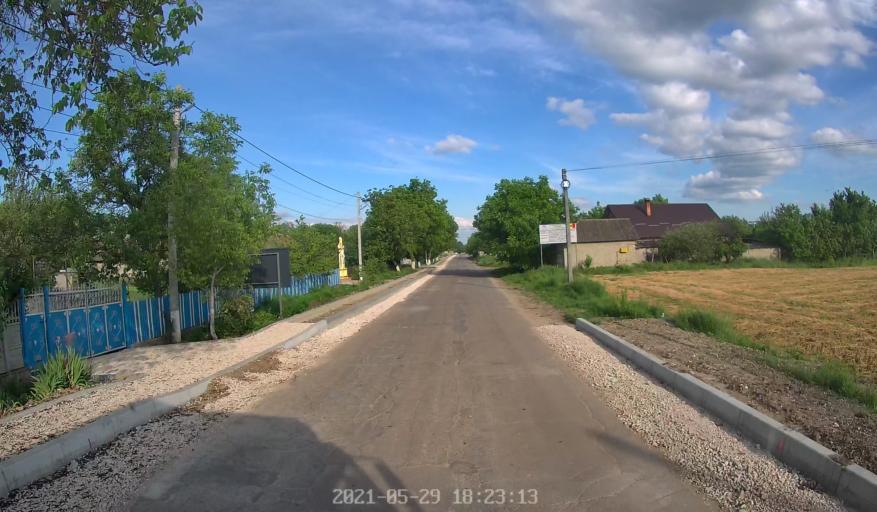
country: MD
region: Laloveni
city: Ialoveni
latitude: 46.8342
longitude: 28.8537
